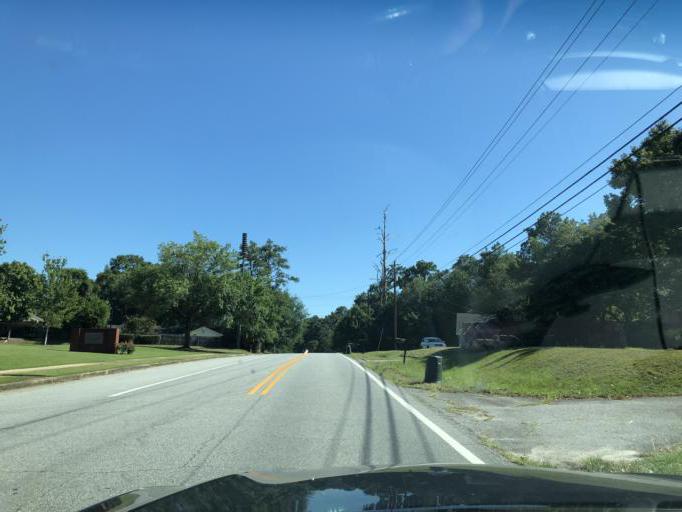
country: US
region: Georgia
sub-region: Muscogee County
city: Columbus
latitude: 32.5057
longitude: -84.9133
